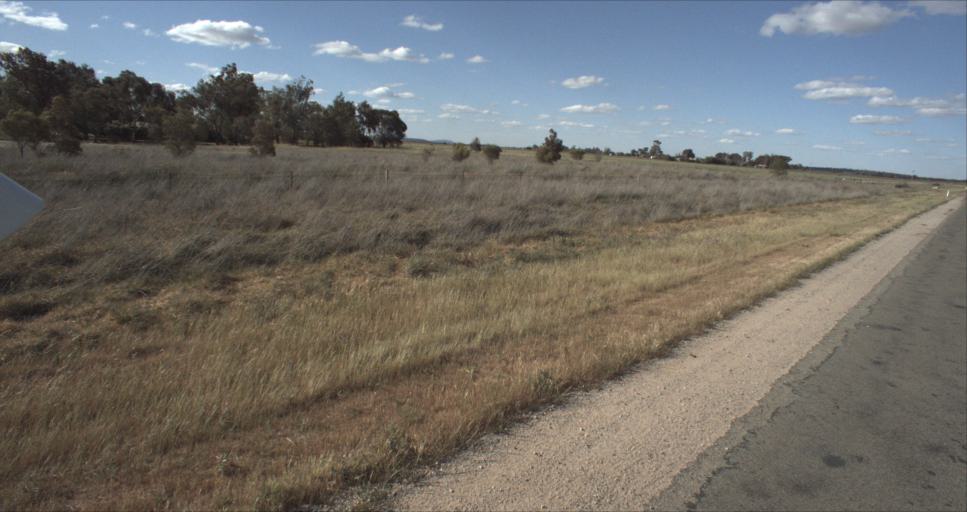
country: AU
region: New South Wales
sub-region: Leeton
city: Leeton
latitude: -34.4576
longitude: 146.2712
